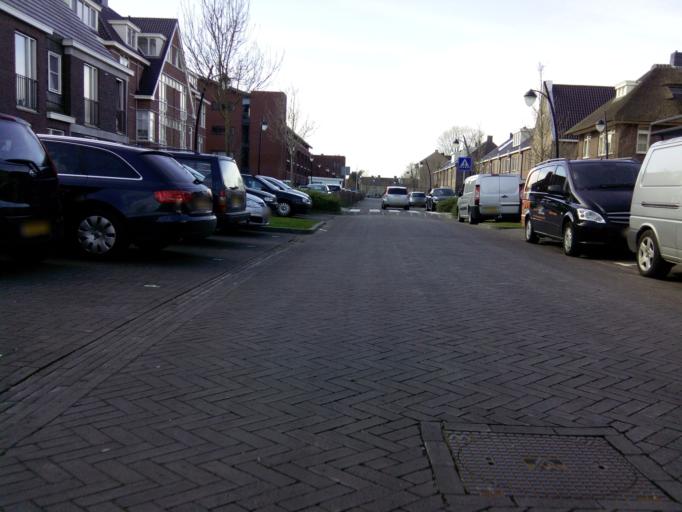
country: NL
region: Utrecht
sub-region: Gemeente Leusden
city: Leusden
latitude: 52.1194
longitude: 5.4112
